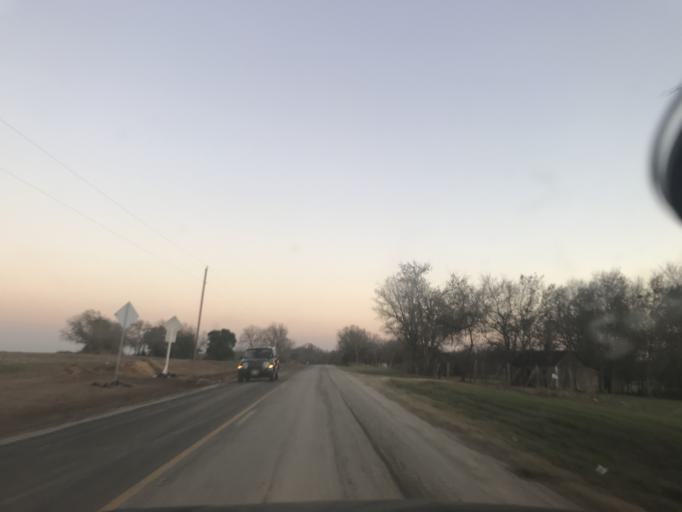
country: US
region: Texas
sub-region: Williamson County
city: Hutto
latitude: 30.5047
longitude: -97.5193
